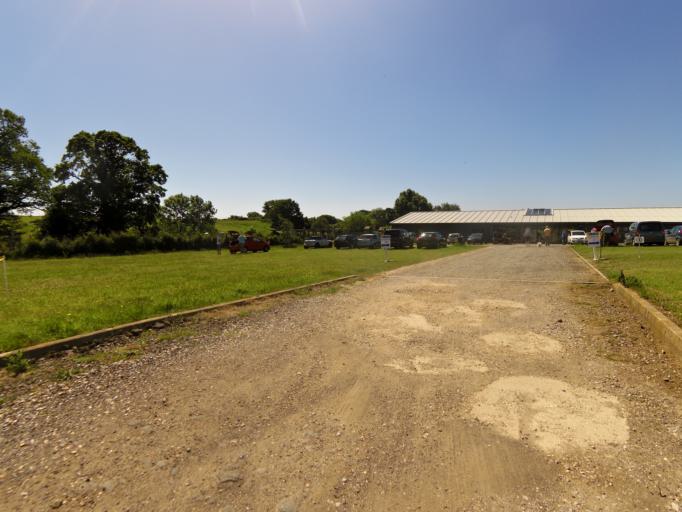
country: GB
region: England
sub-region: Suffolk
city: Wickham Market
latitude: 52.0568
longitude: 1.4465
